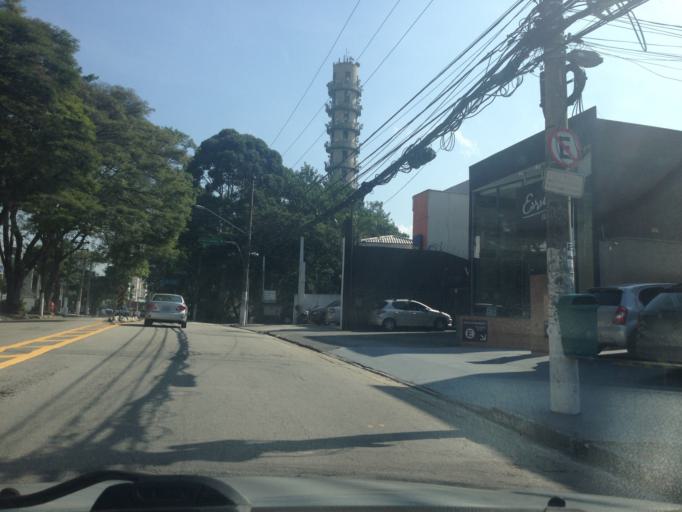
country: BR
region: Sao Paulo
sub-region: Sao Paulo
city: Sao Paulo
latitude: -23.5357
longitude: -46.7105
